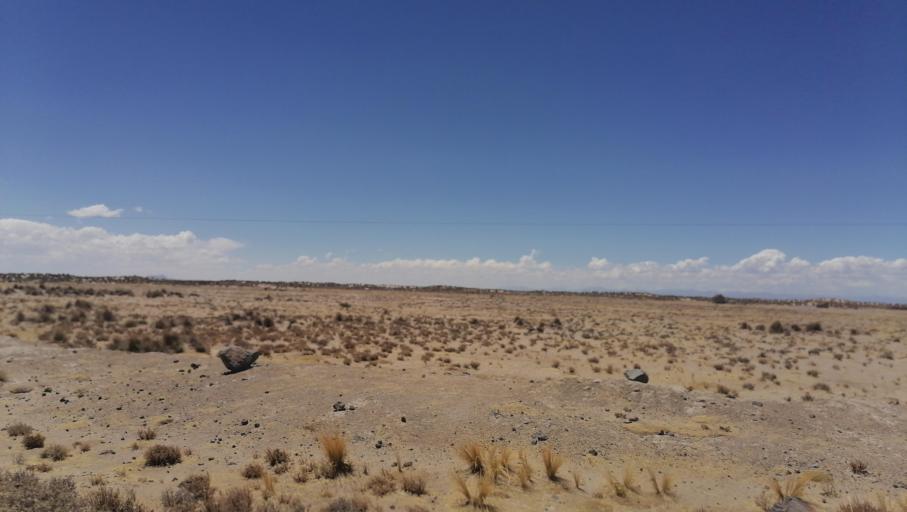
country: BO
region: Oruro
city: Challapata
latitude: -19.2222
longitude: -66.9788
